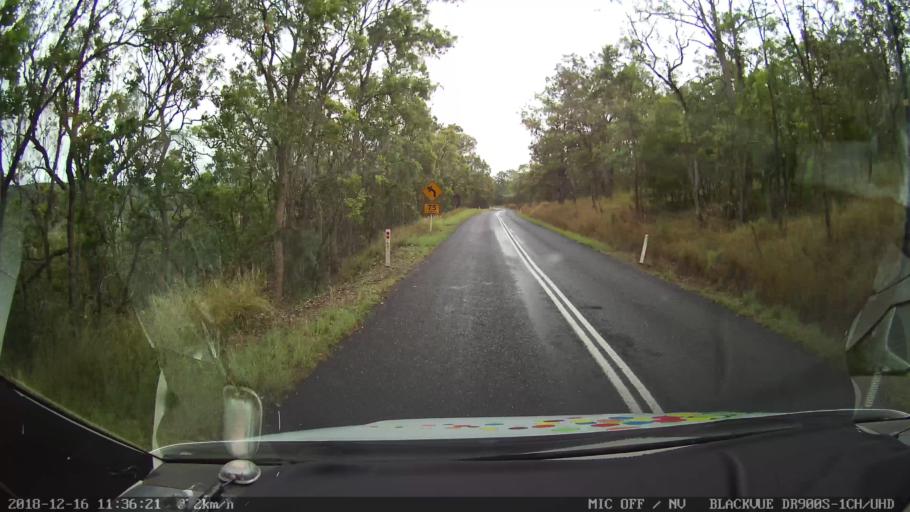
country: AU
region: New South Wales
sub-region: Tenterfield Municipality
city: Carrolls Creek
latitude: -28.9818
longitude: 152.1695
